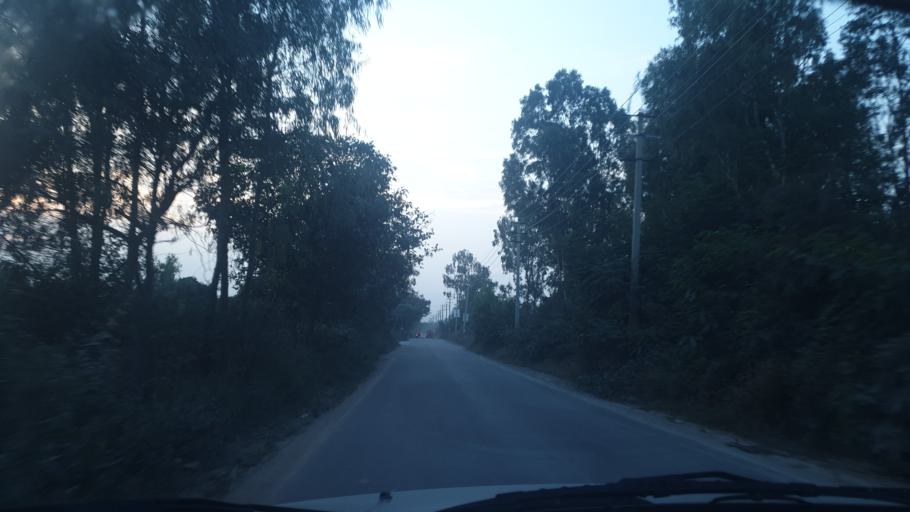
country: IN
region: Karnataka
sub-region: Bangalore Rural
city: Hoskote
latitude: 13.0766
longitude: 77.7019
